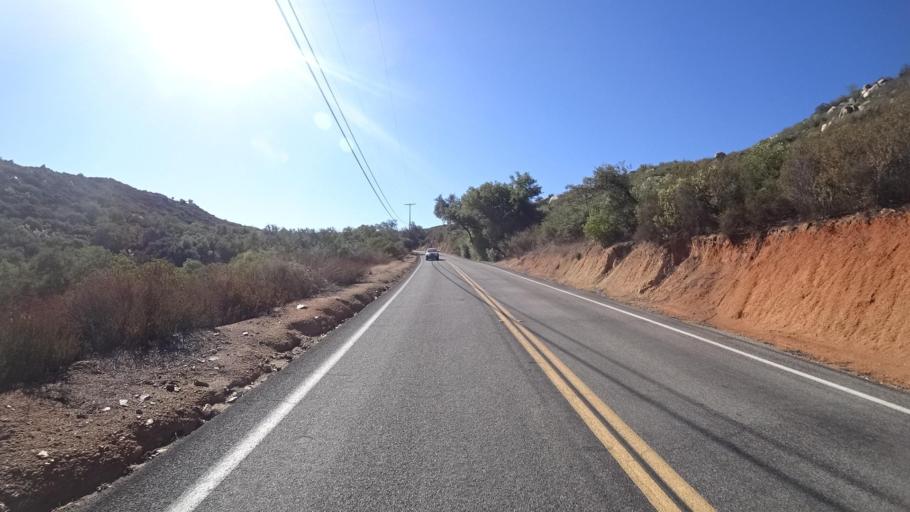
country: US
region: California
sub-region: San Diego County
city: Jamul
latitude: 32.7064
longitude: -116.7479
